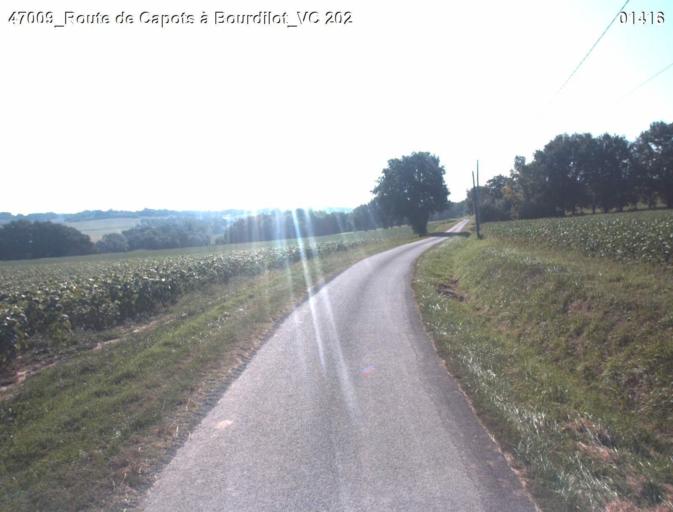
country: FR
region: Aquitaine
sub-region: Departement du Lot-et-Garonne
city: Mezin
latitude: 44.1045
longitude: 0.2952
